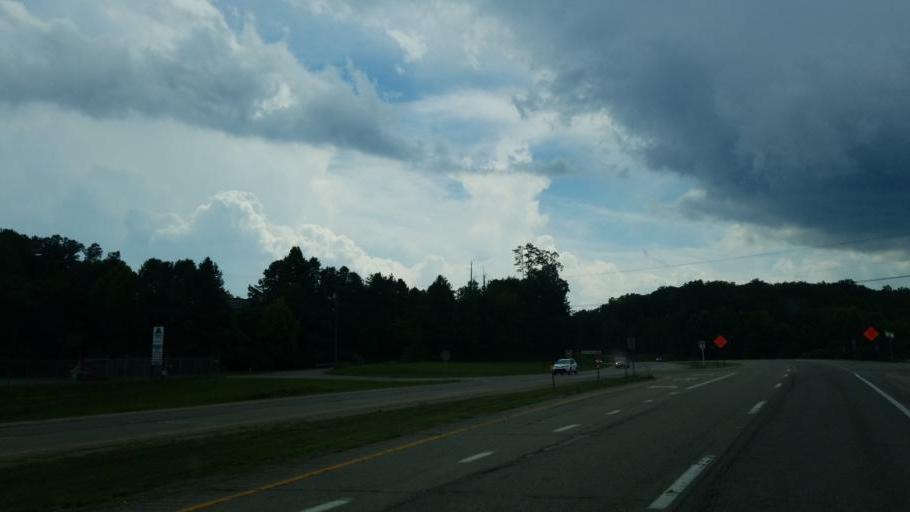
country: US
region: West Virginia
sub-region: Kanawha County
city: Alum Creek
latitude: 38.2769
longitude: -81.7788
